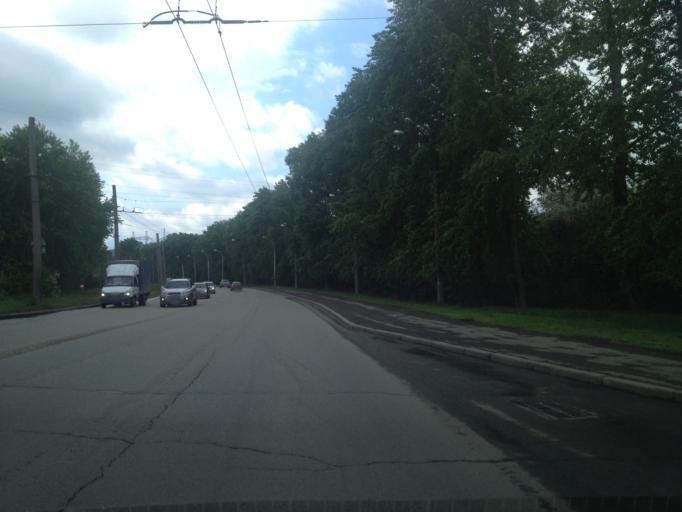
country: RU
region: Sverdlovsk
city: Yekaterinburg
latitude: 56.7615
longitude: 60.6715
